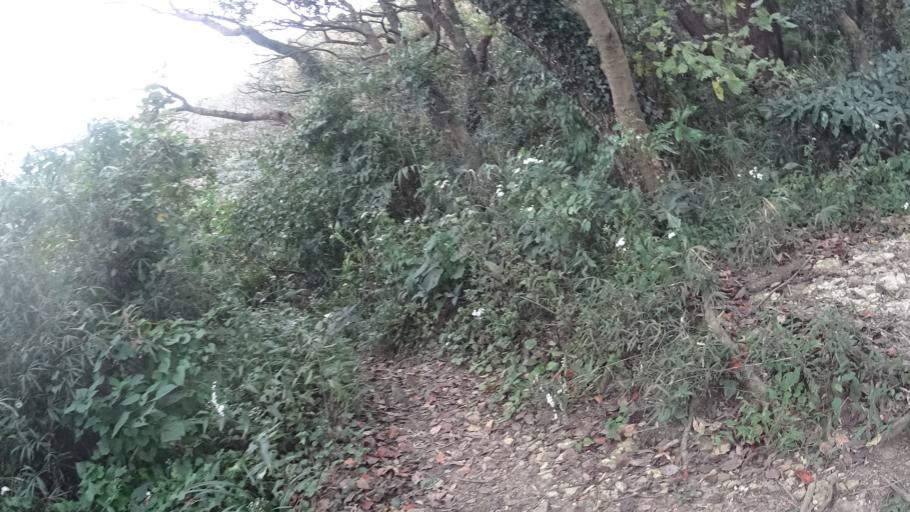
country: JP
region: Kanagawa
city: Zushi
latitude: 35.2892
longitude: 139.6110
